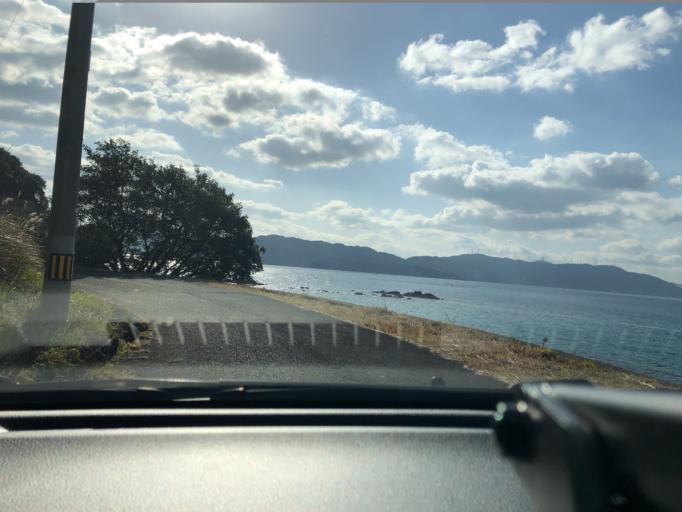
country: JP
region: Kochi
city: Sukumo
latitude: 32.9144
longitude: 132.6881
